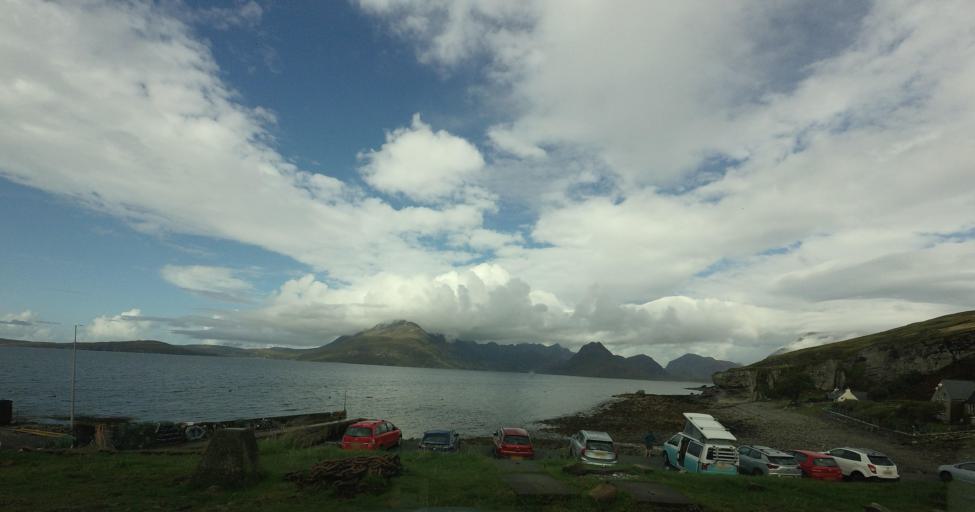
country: GB
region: Scotland
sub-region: Highland
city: Isle of Skye
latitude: 57.1454
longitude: -6.1072
